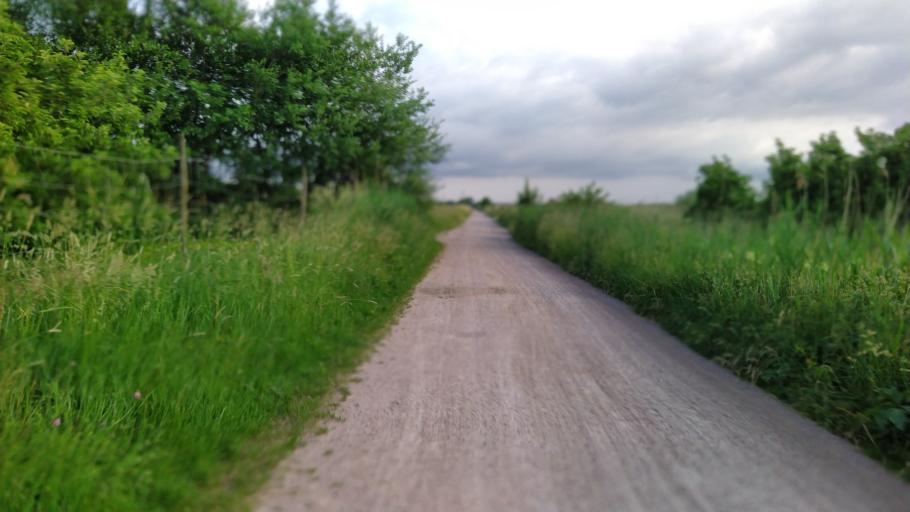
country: DE
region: Lower Saxony
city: Neu Wulmstorf
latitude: 53.5098
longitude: 9.8101
